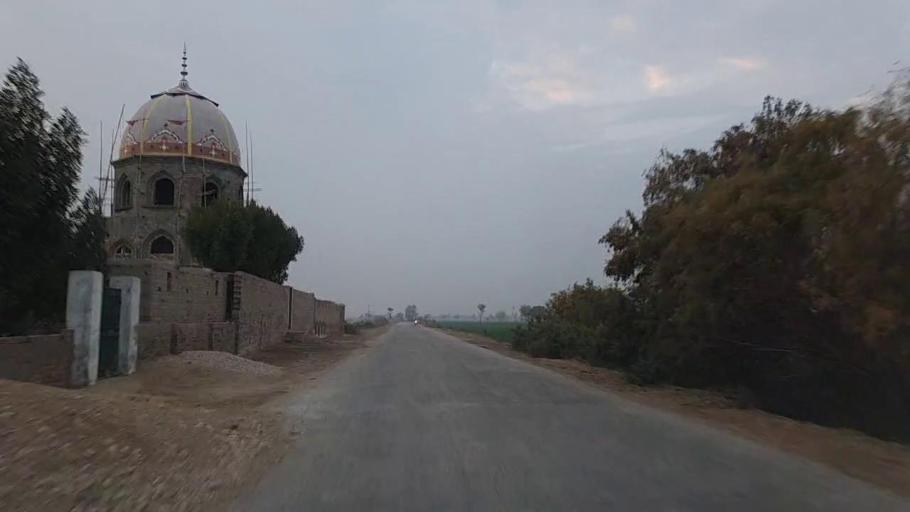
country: PK
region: Sindh
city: Jam Sahib
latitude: 26.3176
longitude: 68.5662
